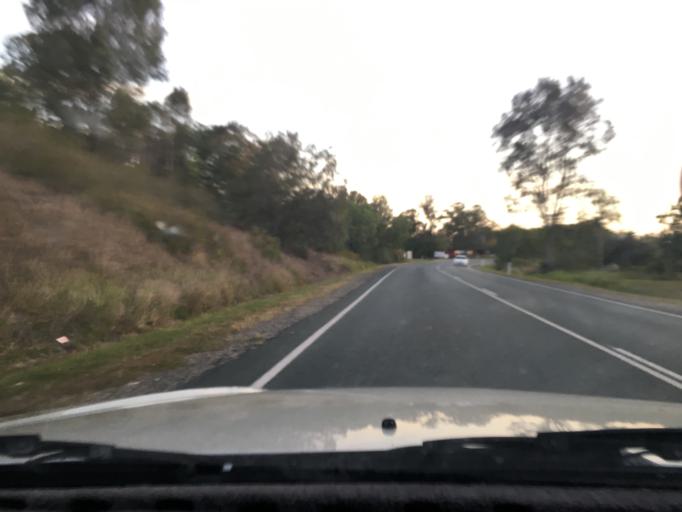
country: AU
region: Queensland
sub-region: Logan
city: Waterford West
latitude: -27.7060
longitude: 153.1473
